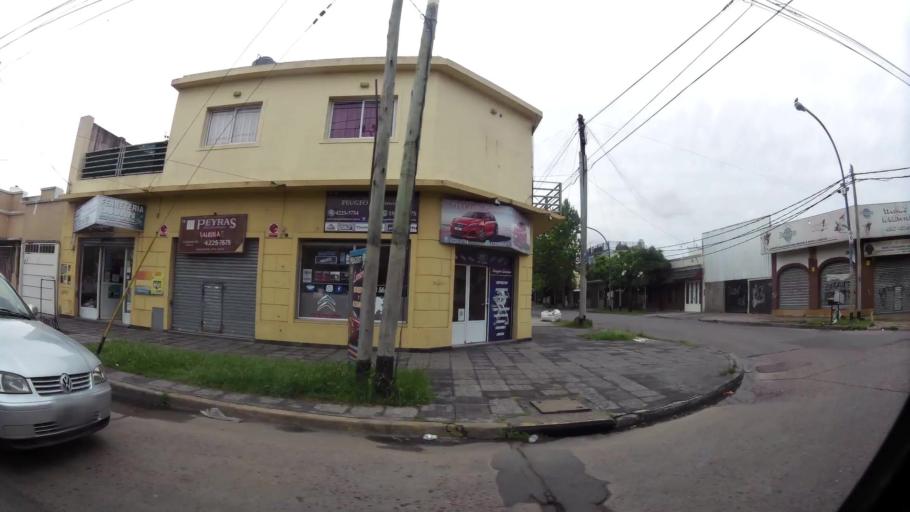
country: AR
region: Buenos Aires
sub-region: Partido de Lanus
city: Lanus
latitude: -34.7167
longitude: -58.3761
